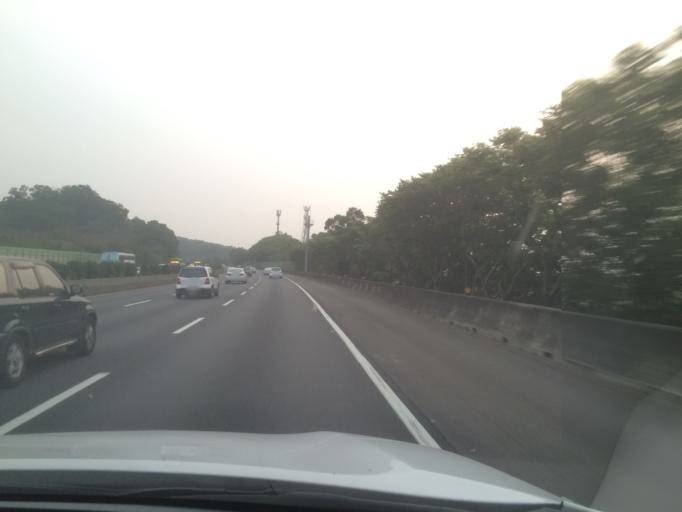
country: TW
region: Taiwan
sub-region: Hsinchu
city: Hsinchu
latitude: 24.7266
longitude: 120.9417
